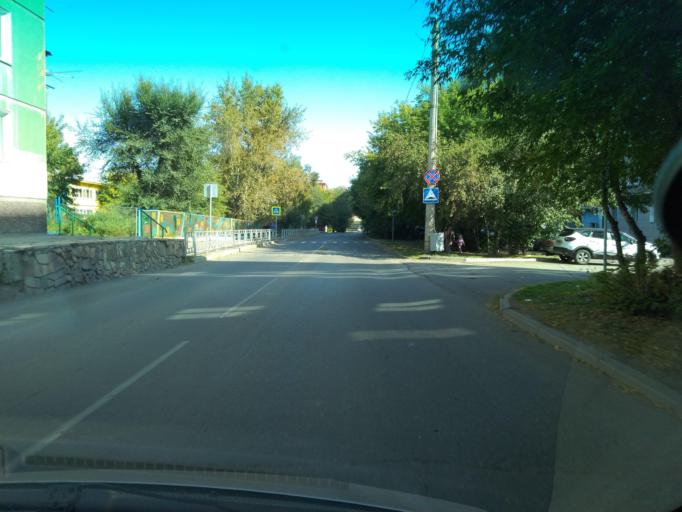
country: RU
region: Krasnoyarskiy
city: Krasnoyarsk
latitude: 56.0061
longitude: 92.9668
